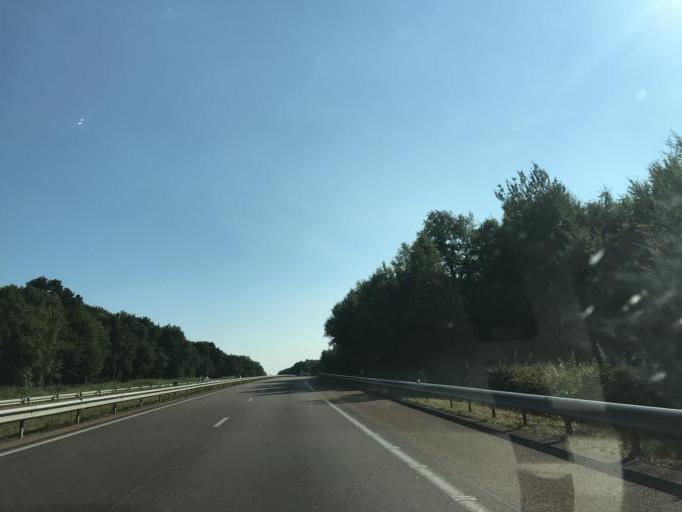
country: FR
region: Bourgogne
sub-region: Departement de Saone-et-Loire
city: Sagy
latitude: 46.6408
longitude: 5.3984
